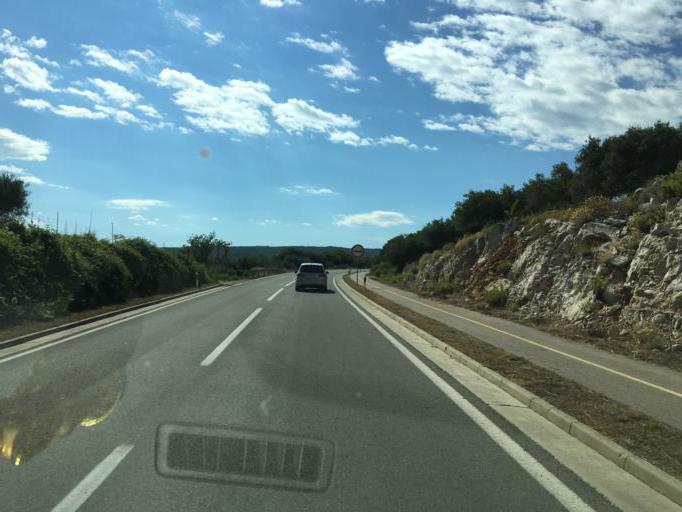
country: HR
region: Primorsko-Goranska
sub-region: Grad Krk
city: Krk
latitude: 45.0338
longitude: 14.5790
